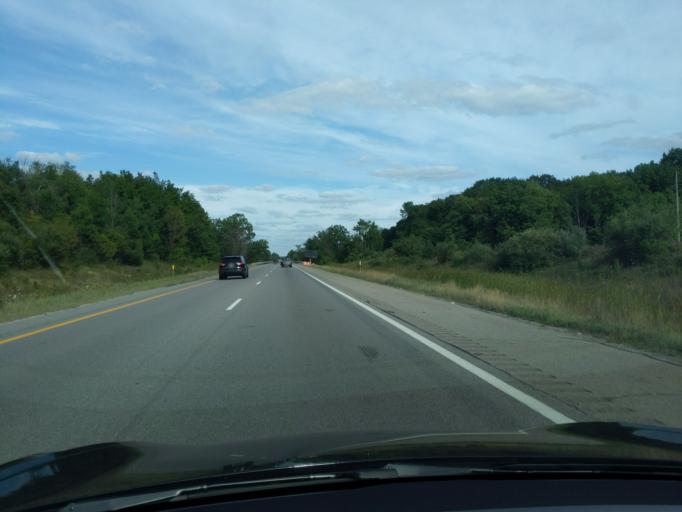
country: US
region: Michigan
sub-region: Ottawa County
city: Coopersville
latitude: 43.0699
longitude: -86.0198
